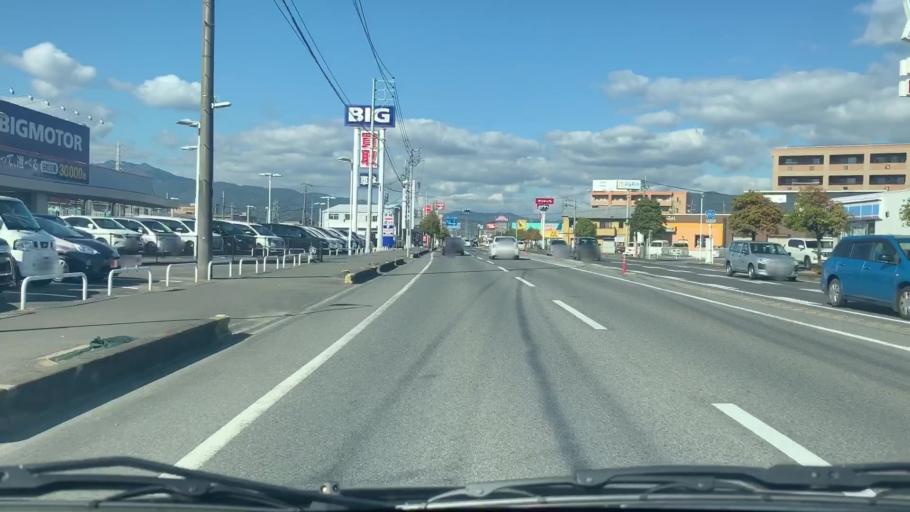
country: JP
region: Saga Prefecture
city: Saga-shi
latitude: 33.2897
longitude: 130.2873
